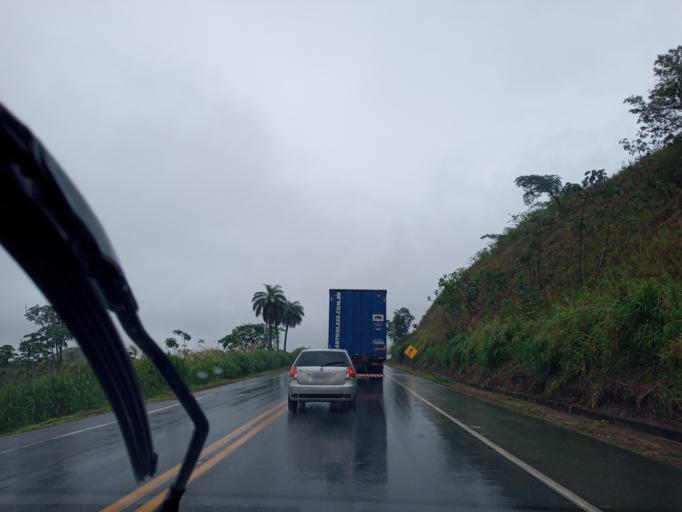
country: BR
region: Minas Gerais
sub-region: Luz
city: Luz
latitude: -19.7215
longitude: -45.8751
